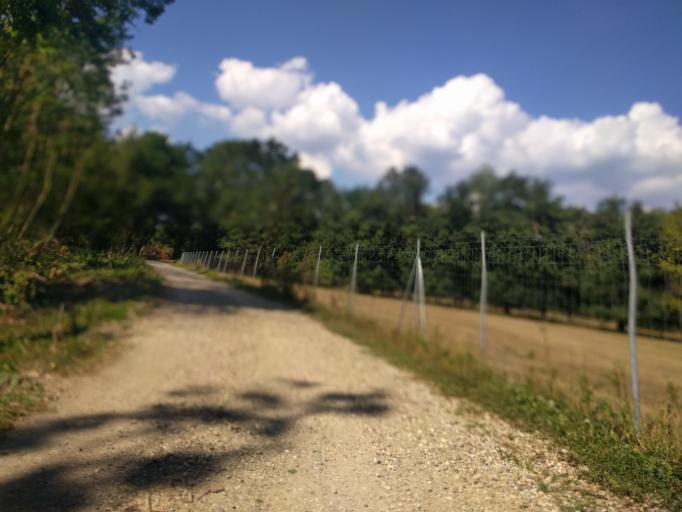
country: DE
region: Bavaria
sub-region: Upper Palatinate
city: Mintraching
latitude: 48.9837
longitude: 12.2753
